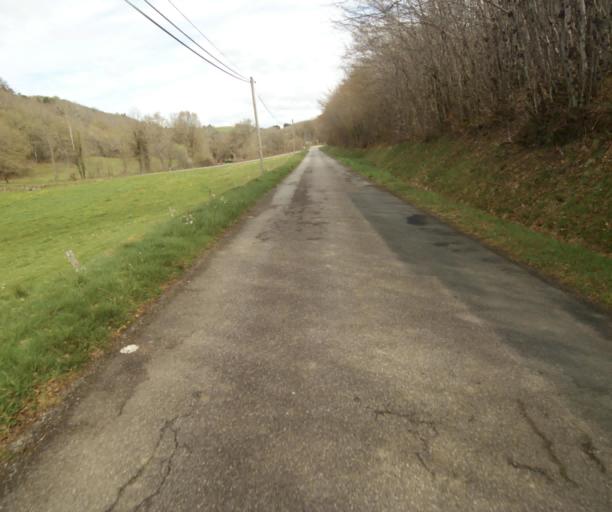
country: FR
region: Limousin
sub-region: Departement de la Correze
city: Laguenne
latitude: 45.2428
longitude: 1.8450
